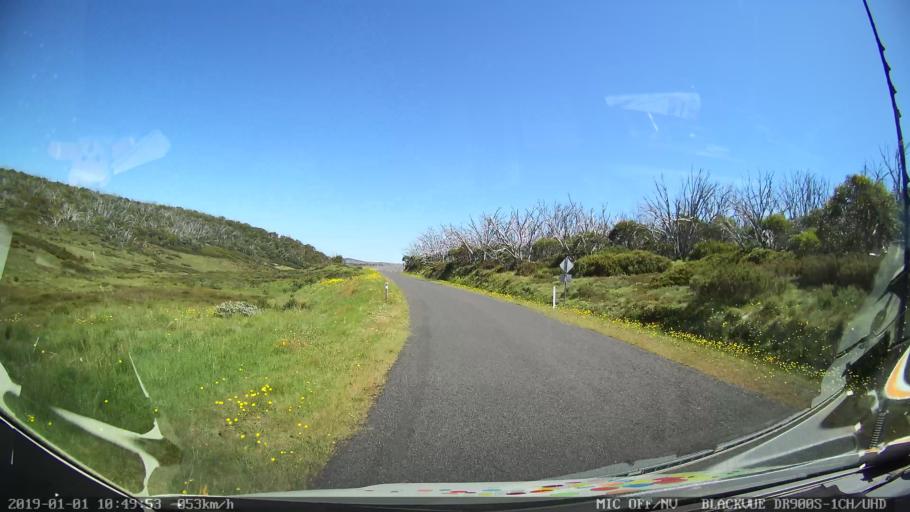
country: AU
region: New South Wales
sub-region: Snowy River
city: Jindabyne
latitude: -36.0327
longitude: 148.3738
